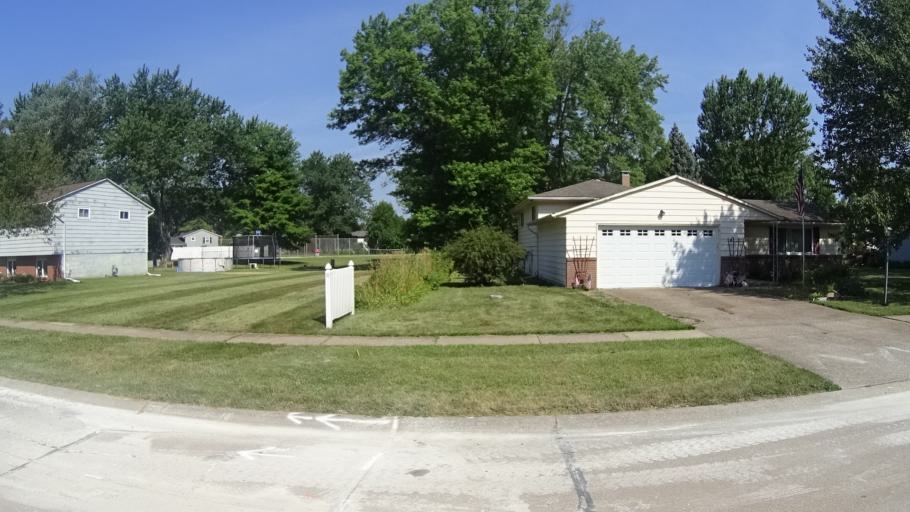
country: US
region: Ohio
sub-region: Erie County
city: Huron
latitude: 41.4012
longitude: -82.5678
